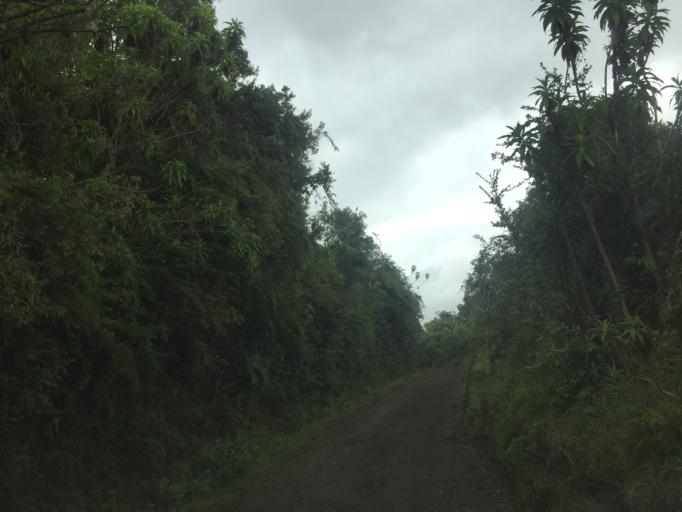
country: EC
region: Imbabura
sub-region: Canton Otavalo
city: Otavalo
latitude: 0.0846
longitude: -78.2970
